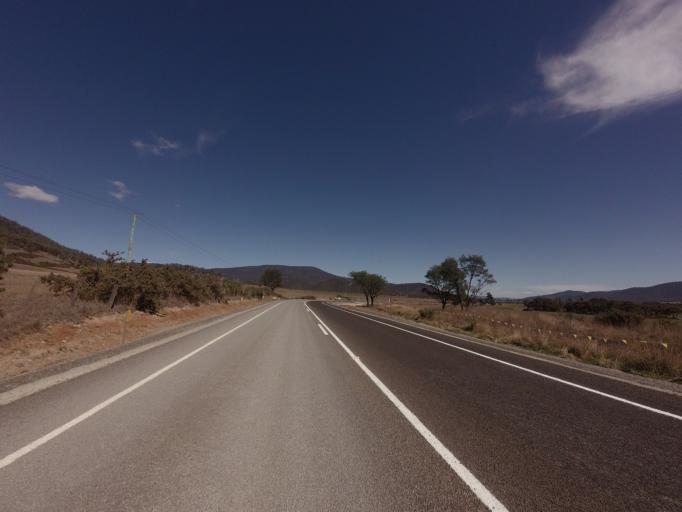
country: AU
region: Tasmania
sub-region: Break O'Day
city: St Helens
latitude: -41.6619
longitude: 147.9140
